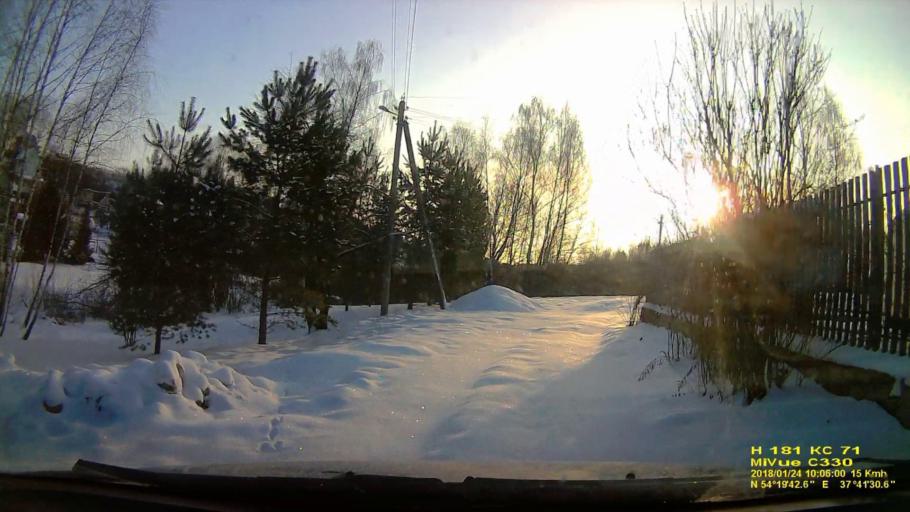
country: RU
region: Tula
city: Revyakino
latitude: 54.3285
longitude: 37.6918
